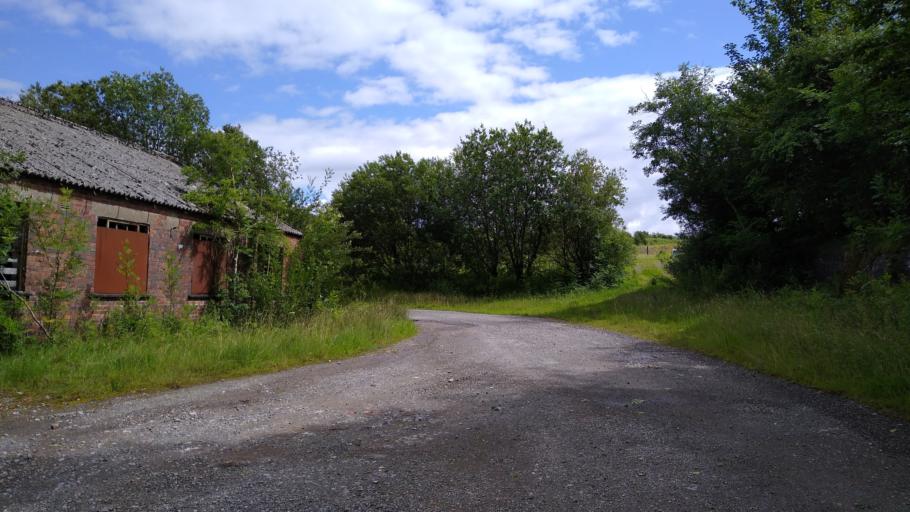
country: GB
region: England
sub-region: Cumbria
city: Aspatria
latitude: 54.7176
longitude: -3.3090
